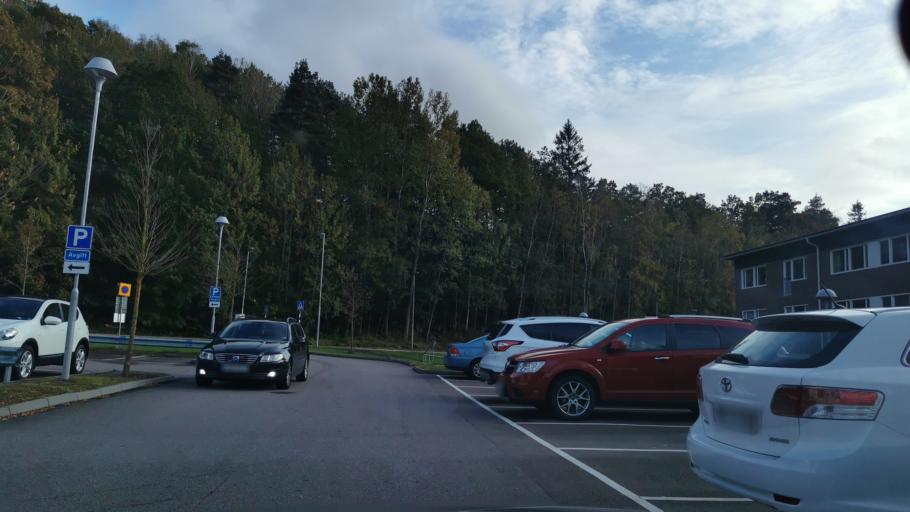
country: SE
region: Vaestra Goetaland
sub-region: Partille Kommun
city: Partille
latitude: 57.7194
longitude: 12.0819
